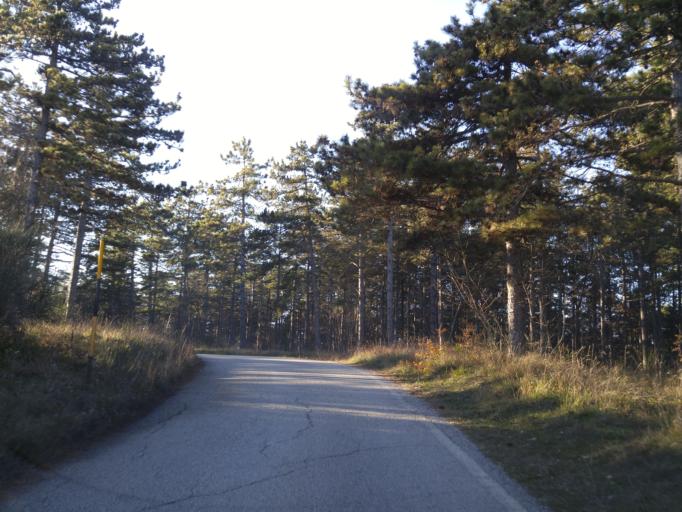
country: IT
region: The Marches
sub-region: Provincia di Pesaro e Urbino
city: Isola del Piano
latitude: 43.7067
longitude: 12.7554
